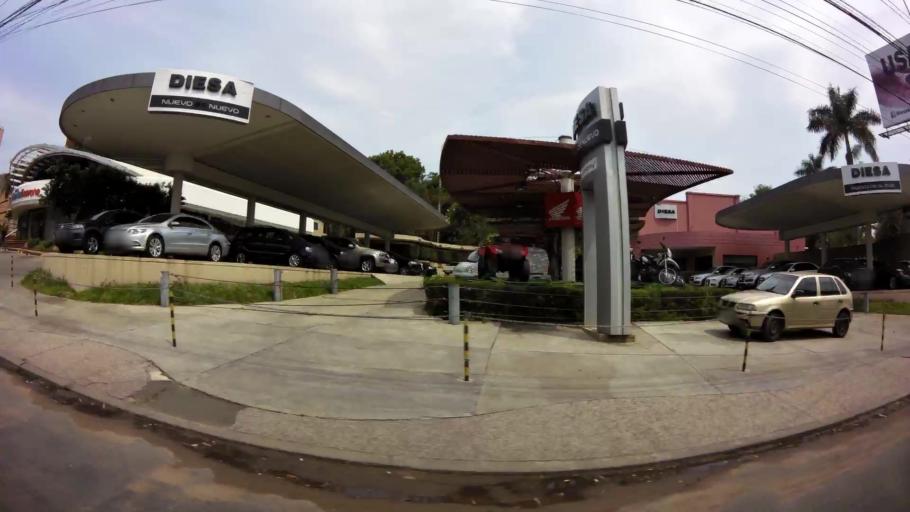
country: PY
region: Asuncion
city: Asuncion
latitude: -25.2861
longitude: -57.5844
